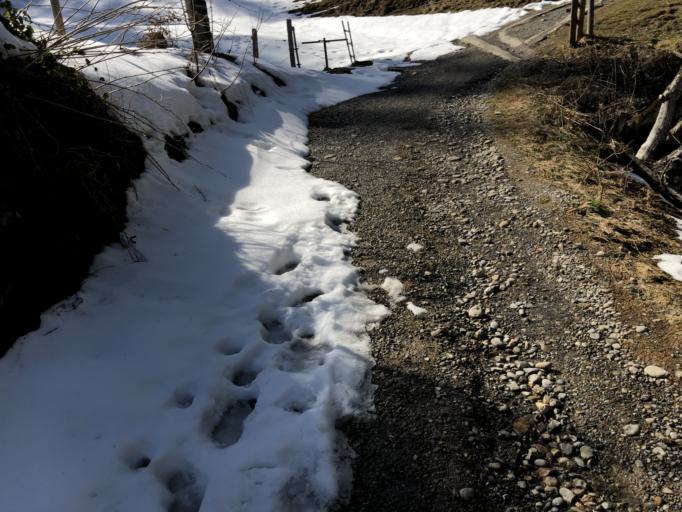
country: CH
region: Appenzell Innerrhoden
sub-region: Appenzell Inner Rhodes
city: Gonten
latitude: 47.3429
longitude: 9.3419
